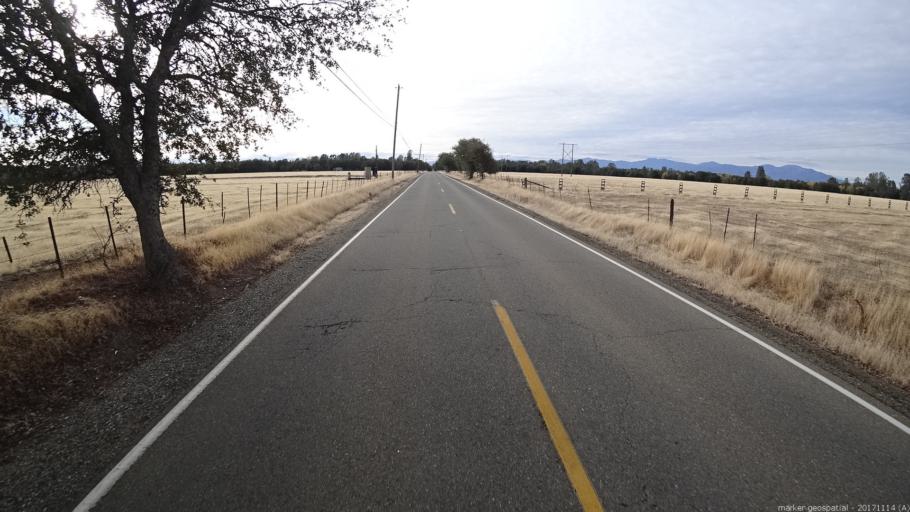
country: US
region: California
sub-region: Shasta County
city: Anderson
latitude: 40.3885
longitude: -122.4164
